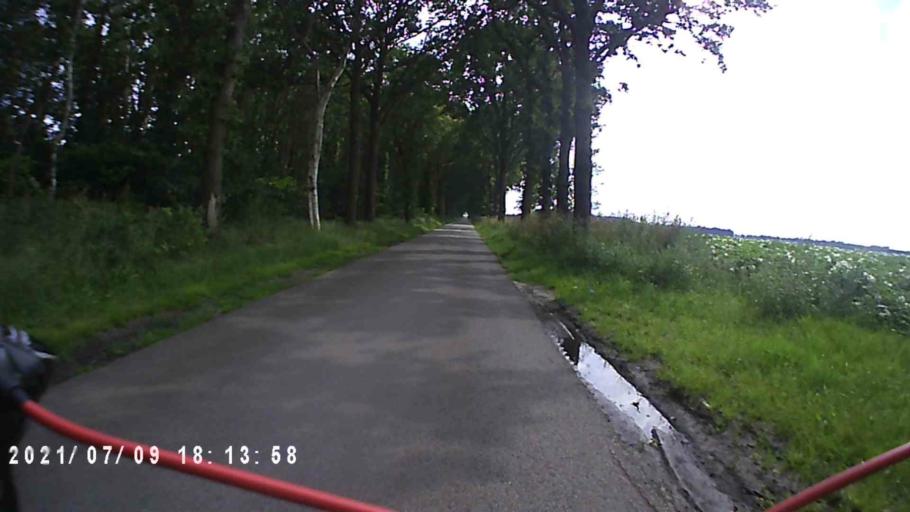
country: NL
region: Groningen
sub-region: Gemeente Pekela
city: Oude Pekela
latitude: 53.0616
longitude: 7.0246
